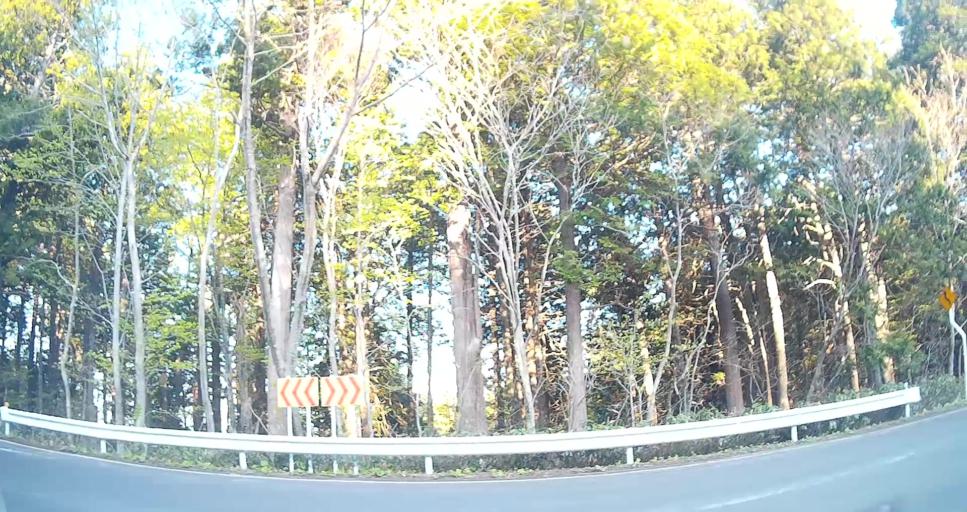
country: JP
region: Aomori
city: Mutsu
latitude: 41.3161
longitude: 141.1122
